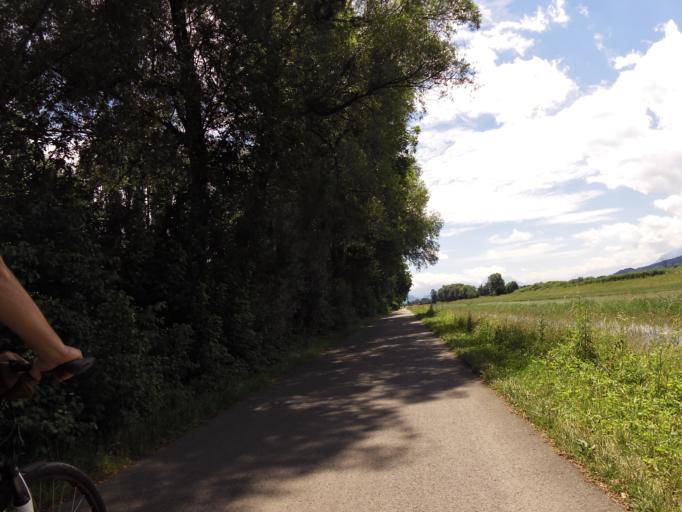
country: AT
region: Vorarlberg
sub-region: Politischer Bezirk Bregenz
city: Hard
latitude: 47.4862
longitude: 9.6753
